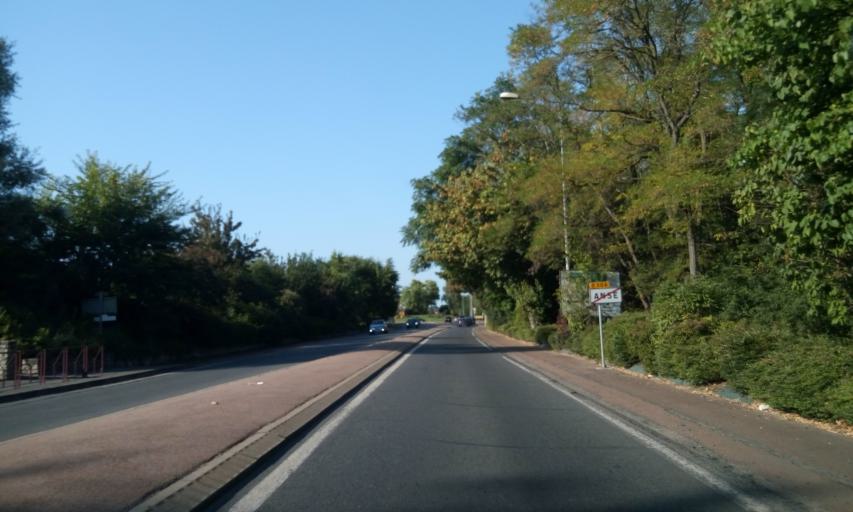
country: FR
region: Rhone-Alpes
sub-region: Departement du Rhone
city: Anse
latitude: 45.9476
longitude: 4.7144
